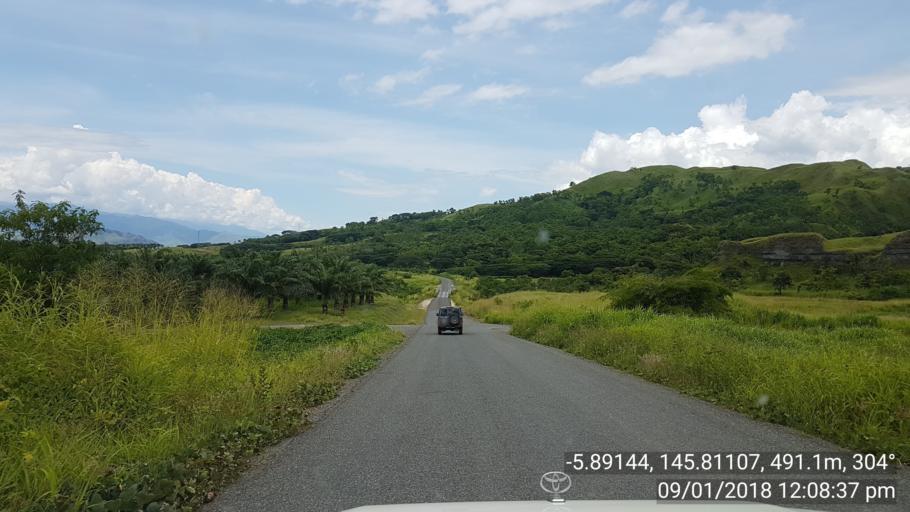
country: PG
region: Eastern Highlands
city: Kainantu
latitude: -5.8915
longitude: 145.8111
